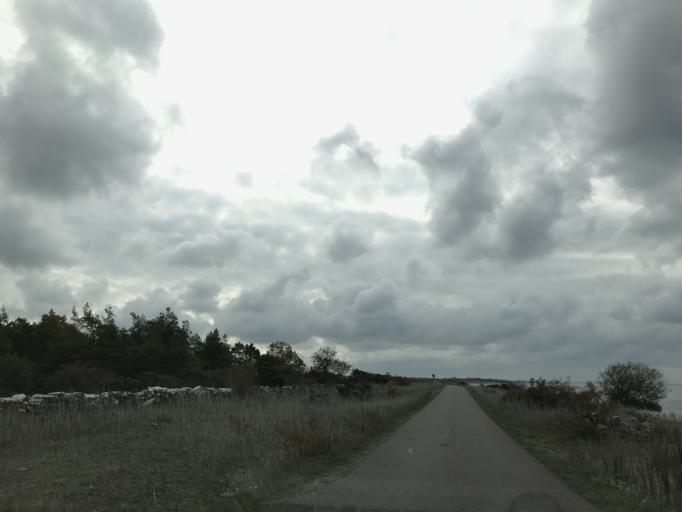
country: SE
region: Kalmar
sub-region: Borgholms Kommun
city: Borgholm
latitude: 57.0574
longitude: 16.8377
